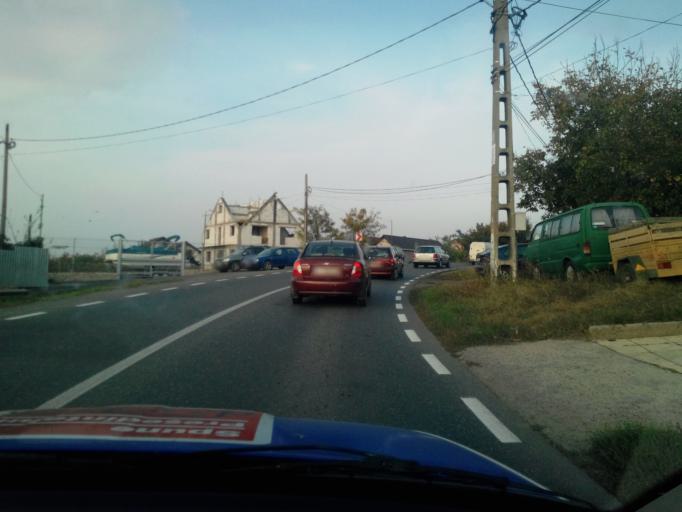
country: RO
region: Tulcea
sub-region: Comuna Somova
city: Mineri
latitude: 45.1690
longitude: 28.7344
